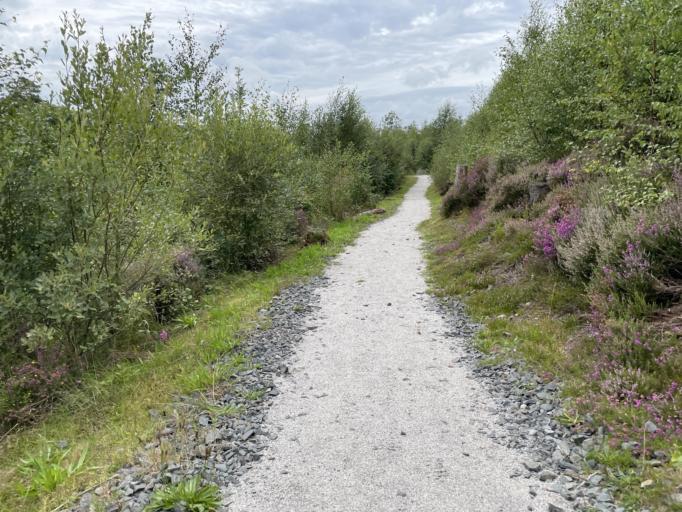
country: GB
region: Scotland
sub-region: Dumfries and Galloway
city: Newton Stewart
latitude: 55.0845
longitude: -4.5029
